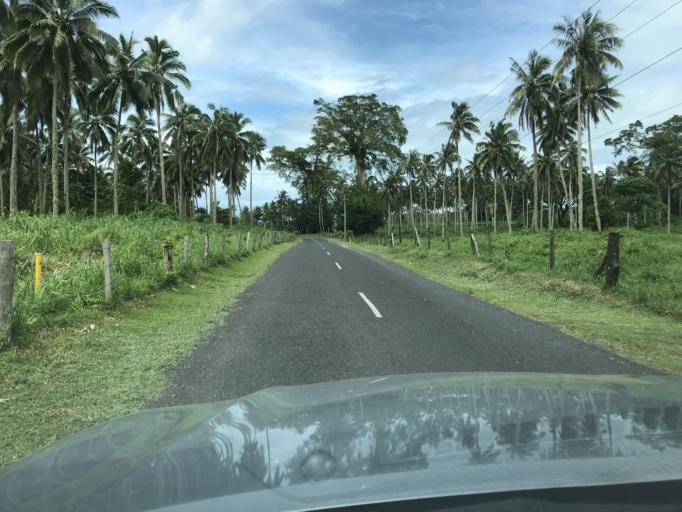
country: WS
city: Fasito`outa
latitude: -13.8713
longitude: -171.9142
